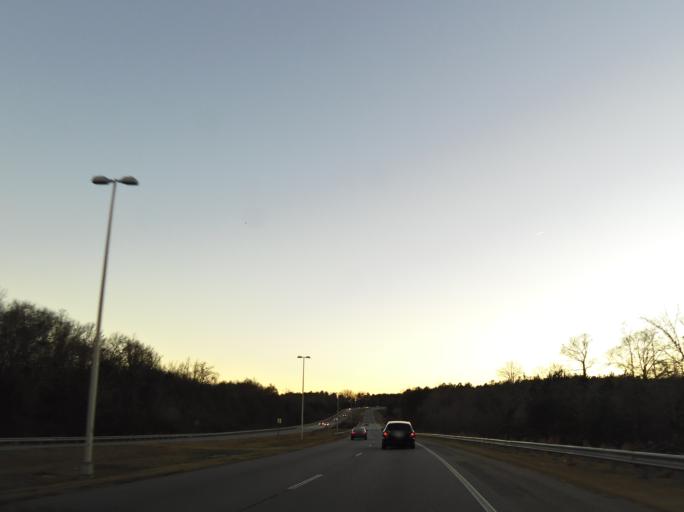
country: US
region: Georgia
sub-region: Houston County
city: Centerville
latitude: 32.5895
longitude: -83.6823
